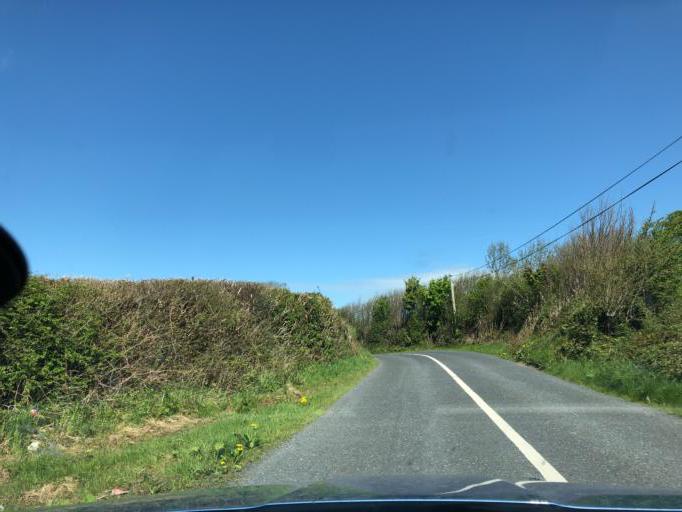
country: IE
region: Connaught
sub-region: County Galway
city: Loughrea
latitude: 53.1590
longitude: -8.3952
